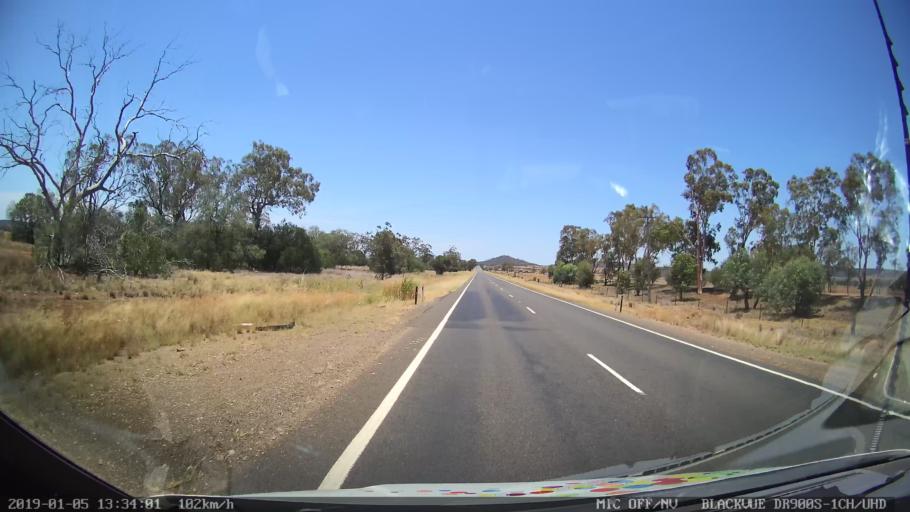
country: AU
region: New South Wales
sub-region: Gunnedah
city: Gunnedah
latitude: -30.9978
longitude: 150.1262
